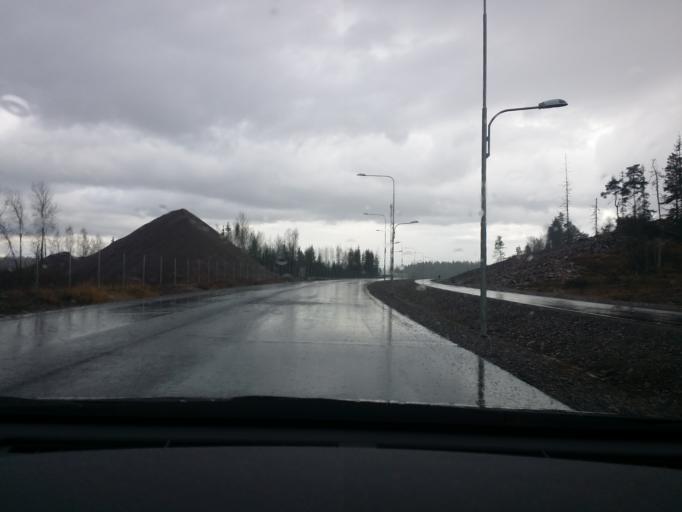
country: SE
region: Soedermanland
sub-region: Eskilstuna Kommun
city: Arla
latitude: 59.3538
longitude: 16.7023
